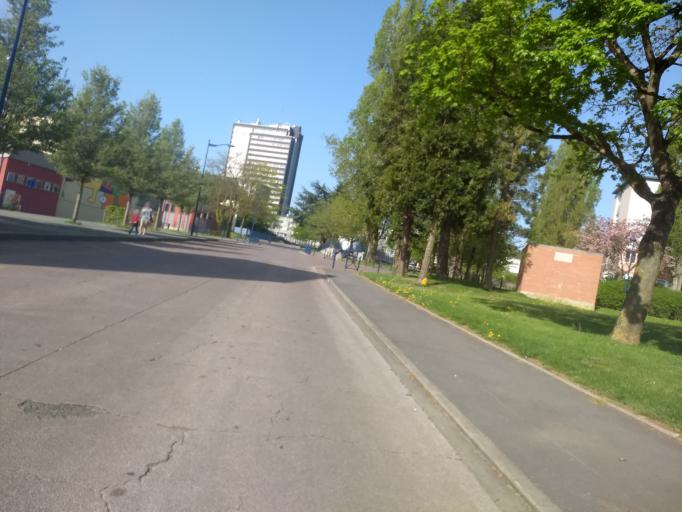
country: FR
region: Nord-Pas-de-Calais
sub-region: Departement du Pas-de-Calais
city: Anzin-Saint-Aubin
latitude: 50.3021
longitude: 2.7496
